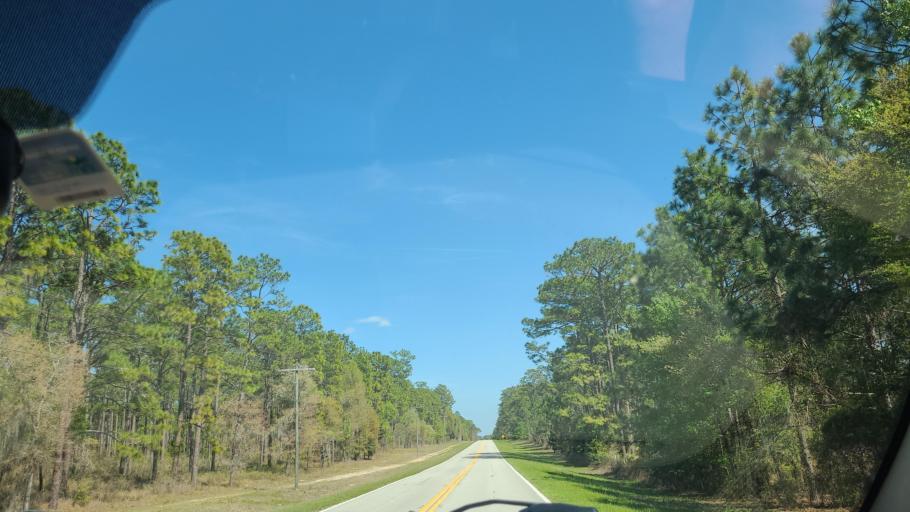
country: US
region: Florida
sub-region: Putnam County
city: Interlachen
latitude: 29.3779
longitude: -81.7908
